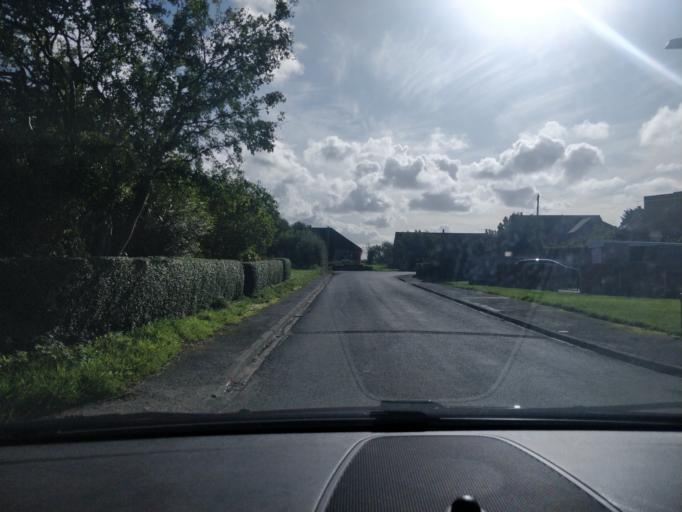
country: GB
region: England
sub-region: Lancashire
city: Banks
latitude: 53.6196
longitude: -2.9385
